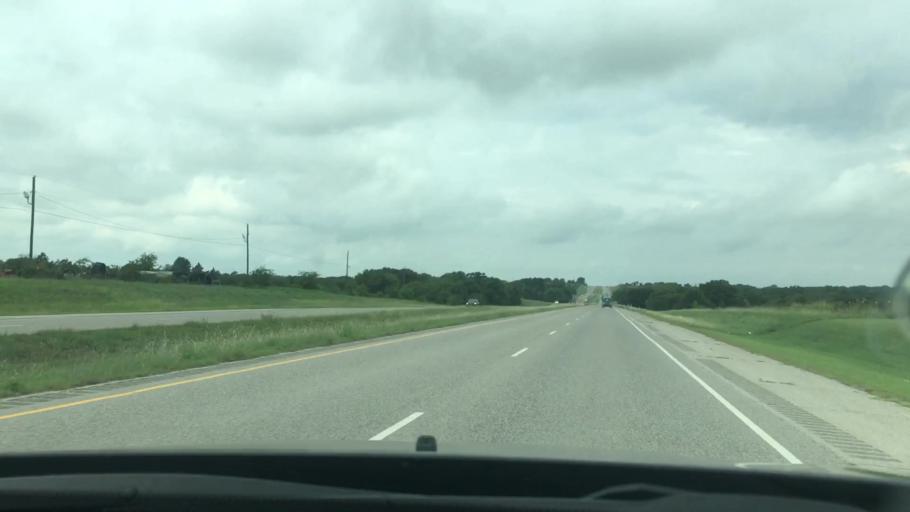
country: US
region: Oklahoma
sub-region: Carter County
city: Wilson
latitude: 34.1730
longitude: -97.4447
